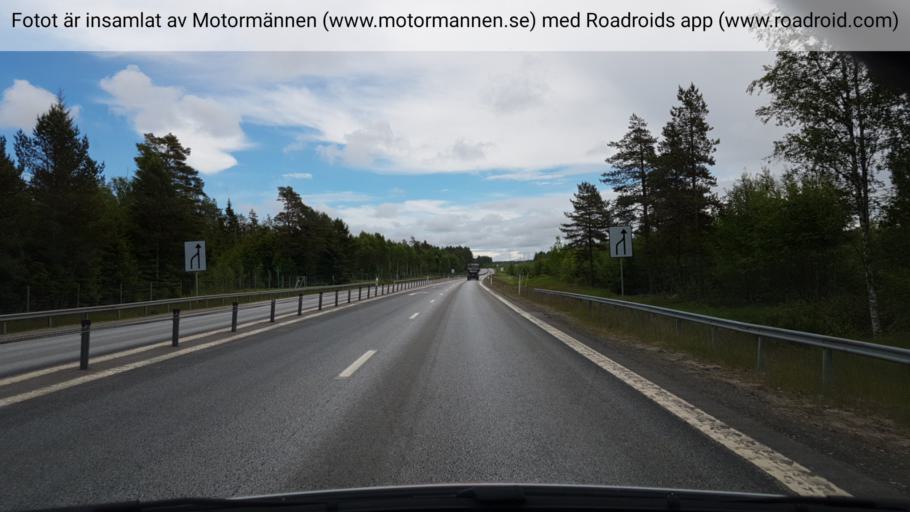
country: SE
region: Vaesterbotten
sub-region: Nordmalings Kommun
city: Nordmaling
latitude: 63.5846
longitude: 19.5678
